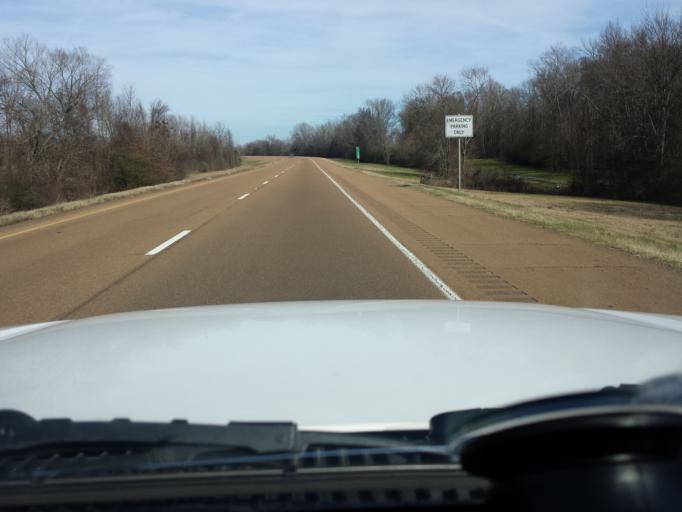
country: US
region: Mississippi
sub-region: Madison County
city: Canton
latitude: 32.6199
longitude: -90.0647
